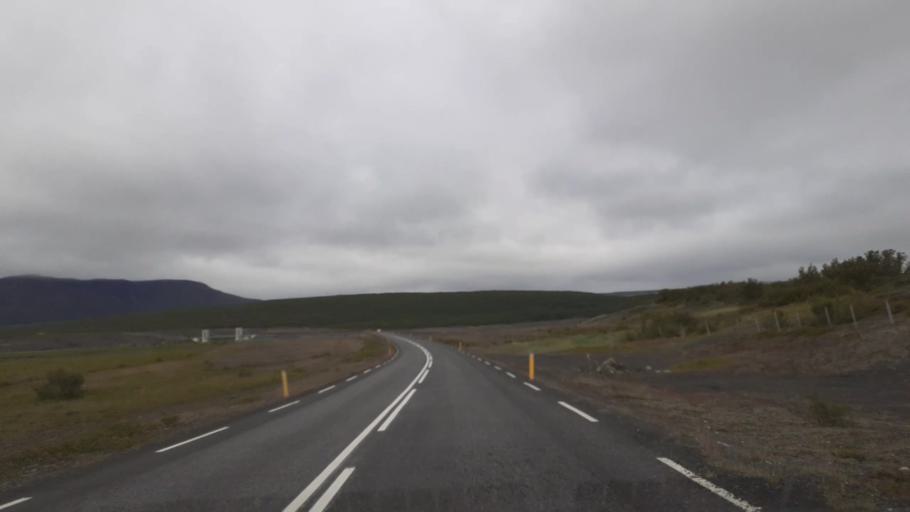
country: IS
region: Northeast
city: Husavik
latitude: 66.0307
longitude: -16.4662
